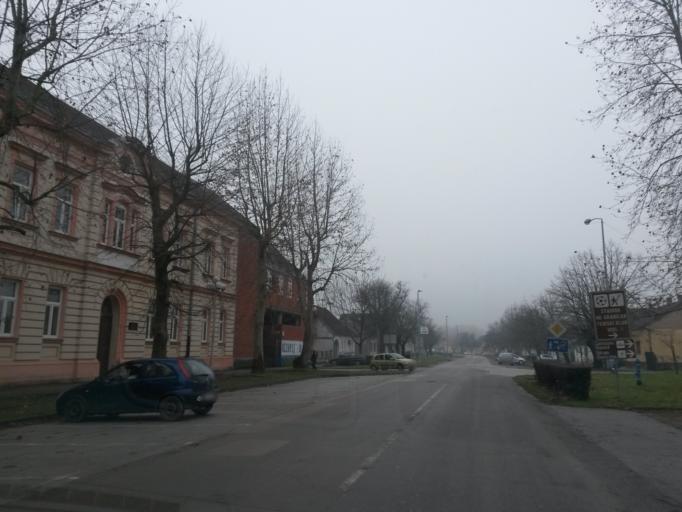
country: HR
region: Vukovarsko-Srijemska
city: Zupanja
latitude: 45.0724
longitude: 18.6914
